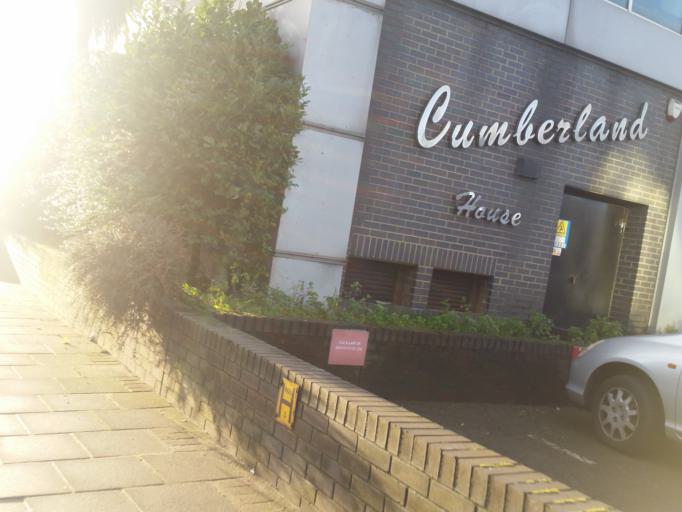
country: GB
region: England
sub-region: Greater London
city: Hammersmith
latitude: 51.5286
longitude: -0.2363
